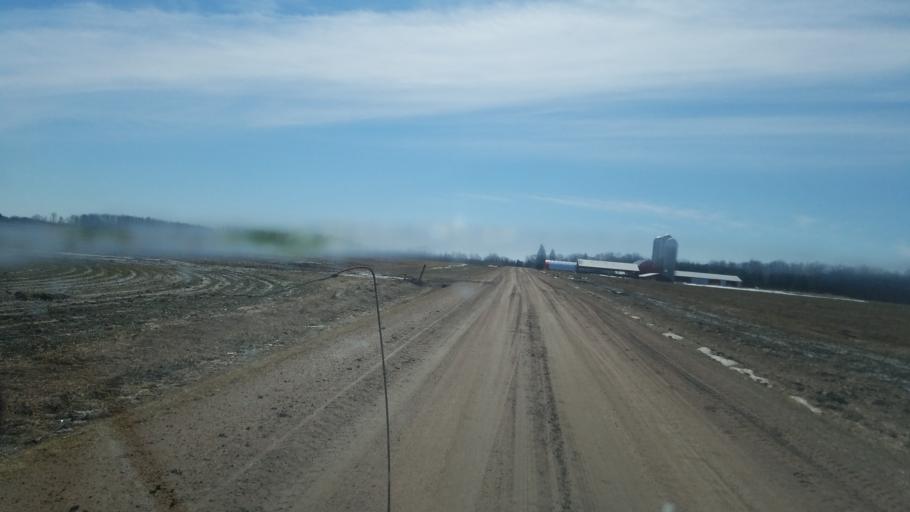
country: US
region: Wisconsin
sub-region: Clark County
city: Loyal
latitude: 44.6369
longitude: -90.4073
